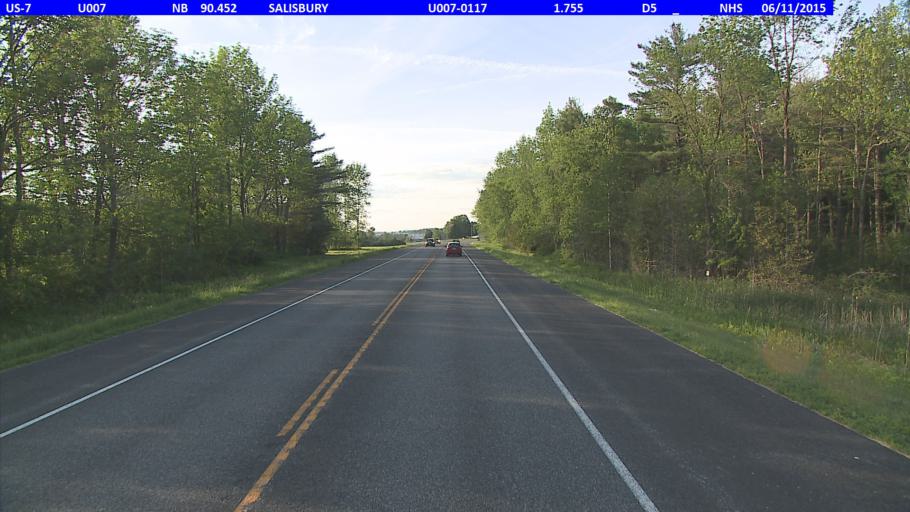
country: US
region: Vermont
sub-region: Addison County
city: Middlebury (village)
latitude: 43.9182
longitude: -73.1116
